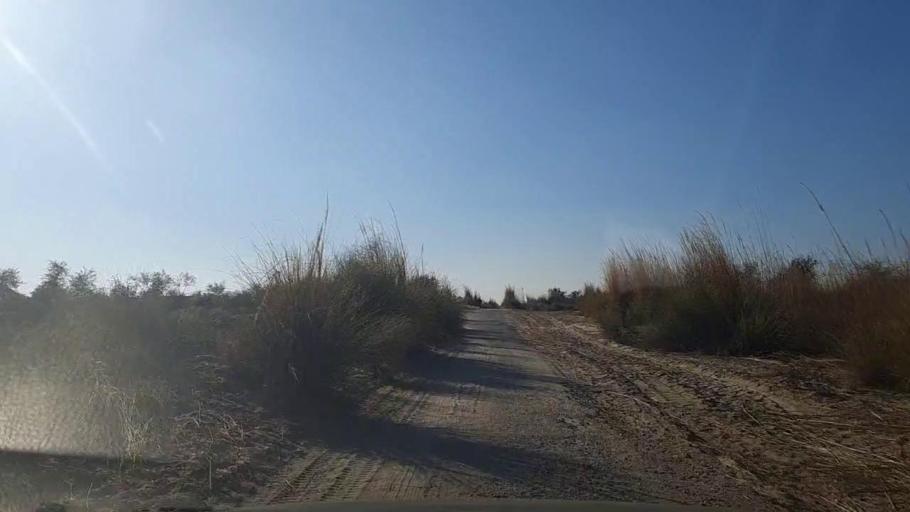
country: PK
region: Sindh
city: Khadro
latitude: 26.2412
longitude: 68.8710
